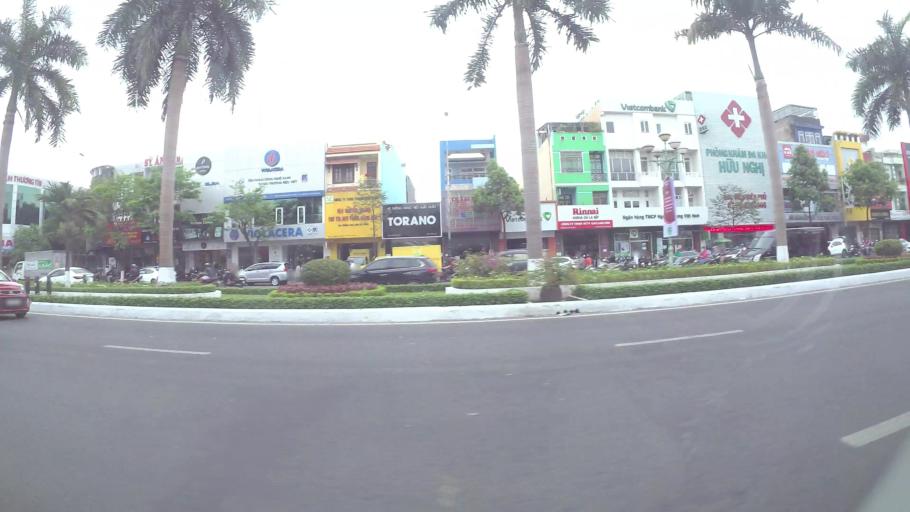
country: VN
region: Da Nang
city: Thanh Khe
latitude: 16.0660
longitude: 108.1933
